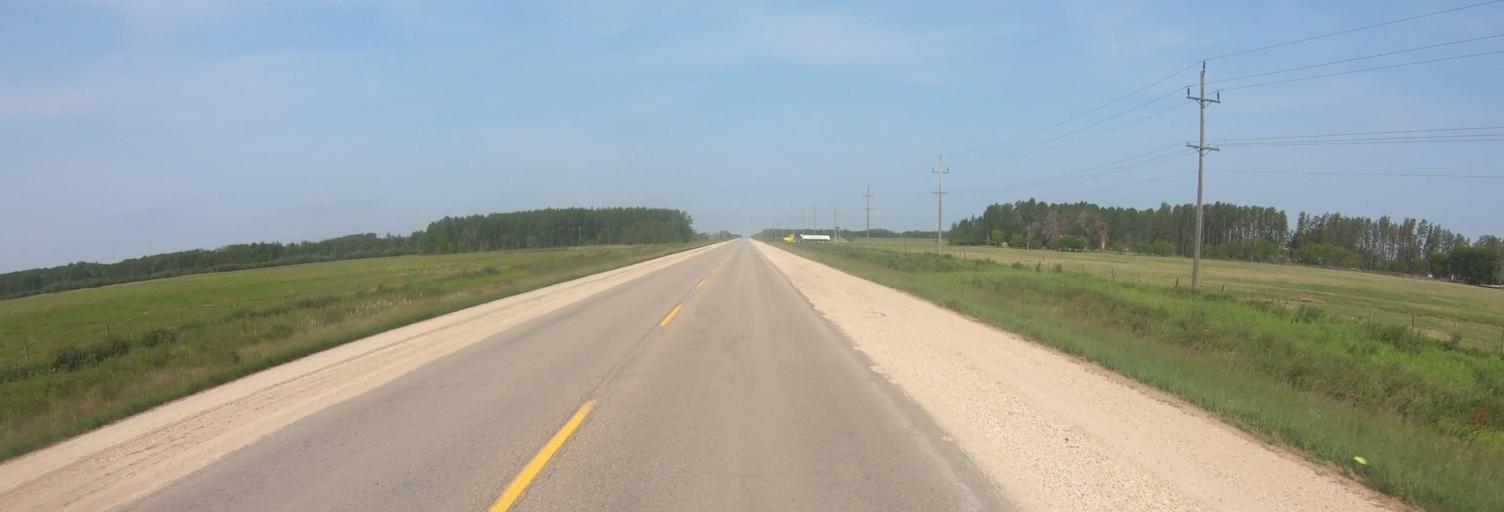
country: CA
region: Manitoba
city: La Broquerie
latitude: 49.3017
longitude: -96.5478
